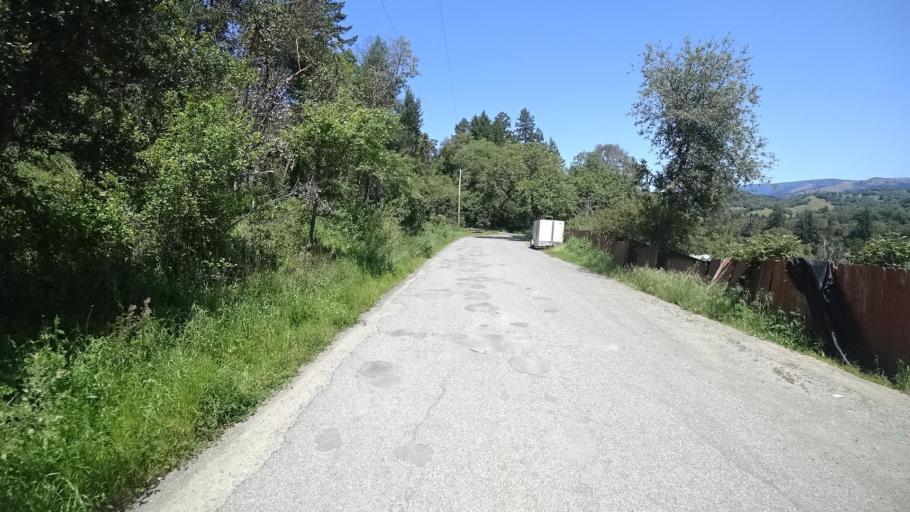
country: US
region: California
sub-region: Humboldt County
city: Redway
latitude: 40.1688
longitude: -123.6049
